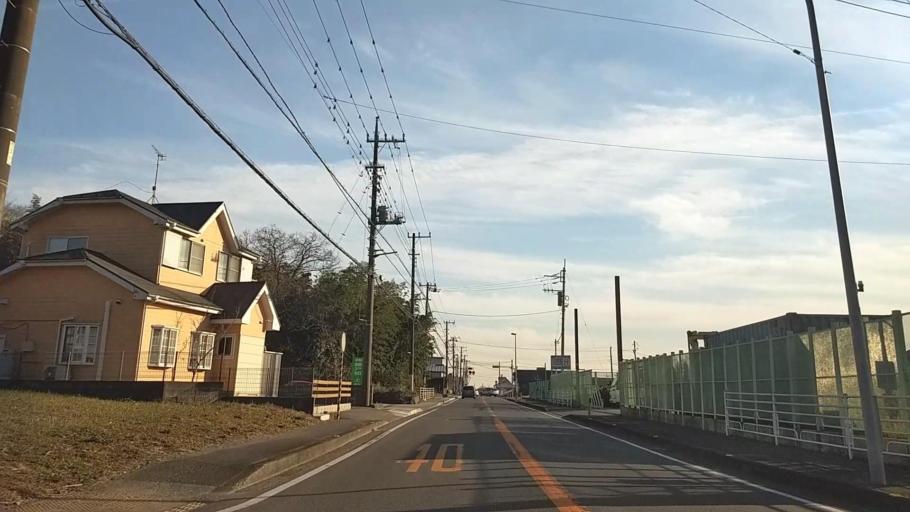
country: JP
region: Kanagawa
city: Zama
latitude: 35.5058
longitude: 139.3092
